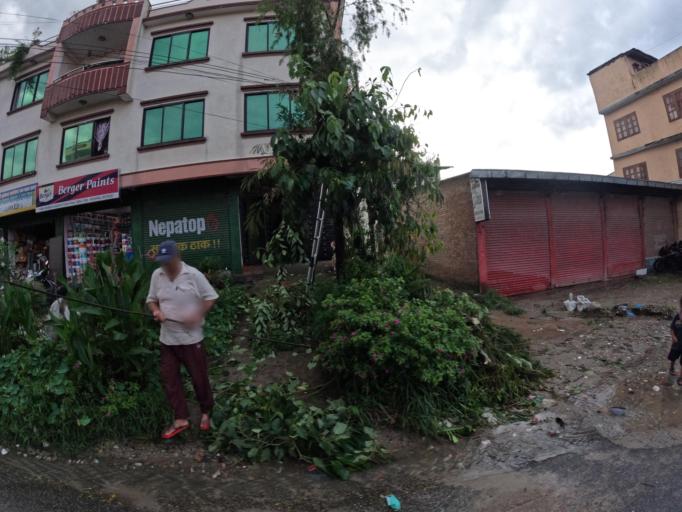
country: NP
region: Central Region
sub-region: Bagmati Zone
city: Kathmandu
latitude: 27.7632
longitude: 85.3306
